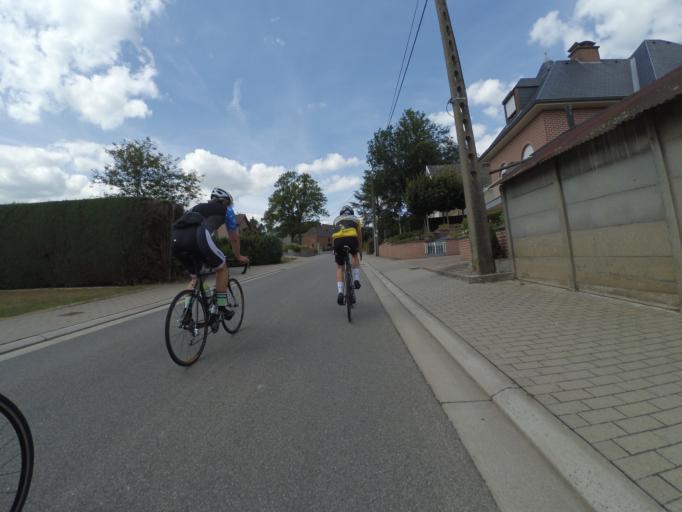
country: BE
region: Flanders
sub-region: Provincie Oost-Vlaanderen
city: Zottegem
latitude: 50.8494
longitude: 3.7558
